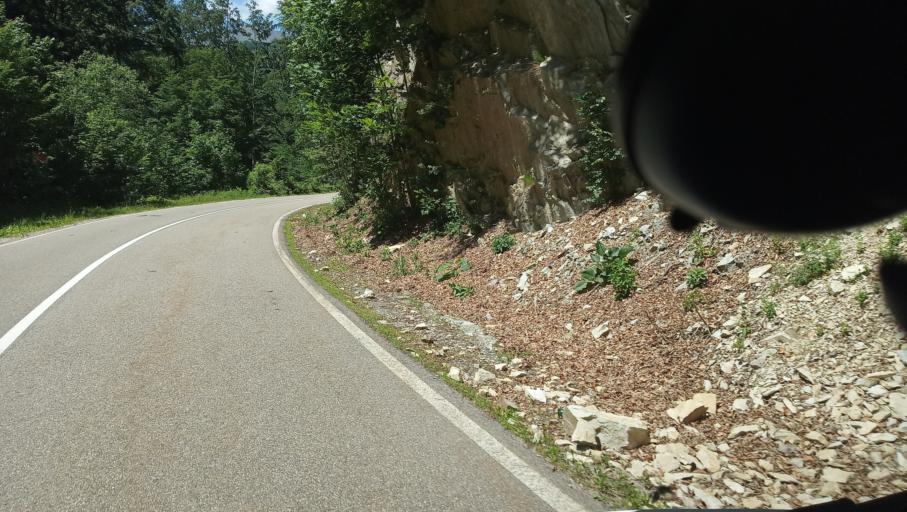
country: RO
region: Mehedinti
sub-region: Comuna Isverna
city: Isverna
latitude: 45.0534
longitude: 22.6183
